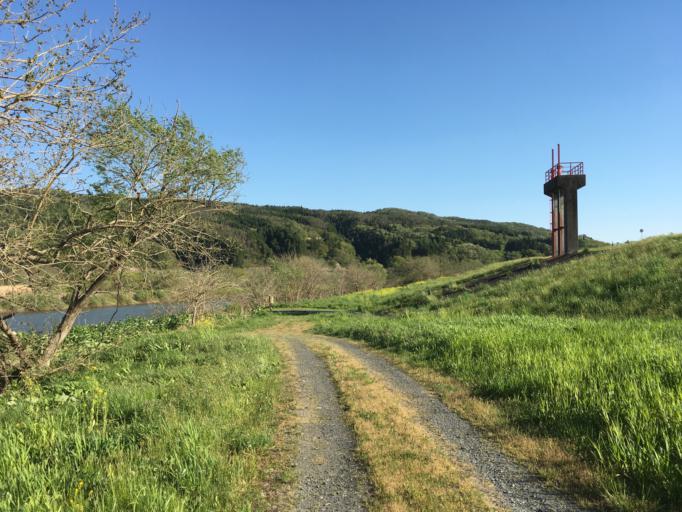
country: JP
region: Iwate
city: Ichinoseki
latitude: 38.8364
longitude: 141.2597
